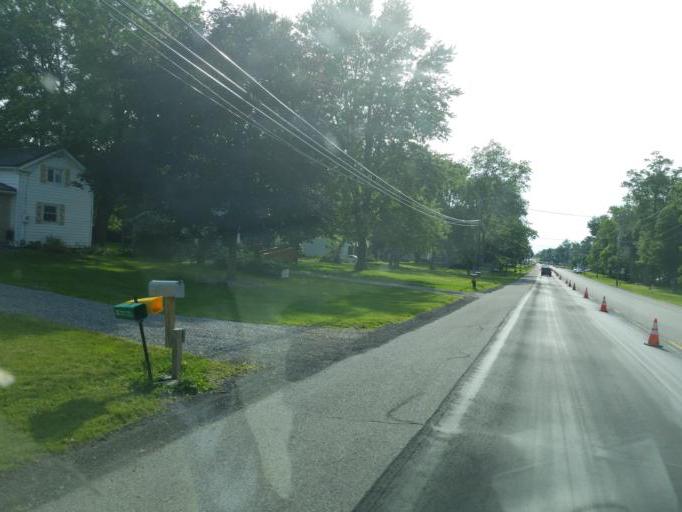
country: US
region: New York
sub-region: Genesee County
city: Le Roy
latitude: 42.9811
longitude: -78.0701
